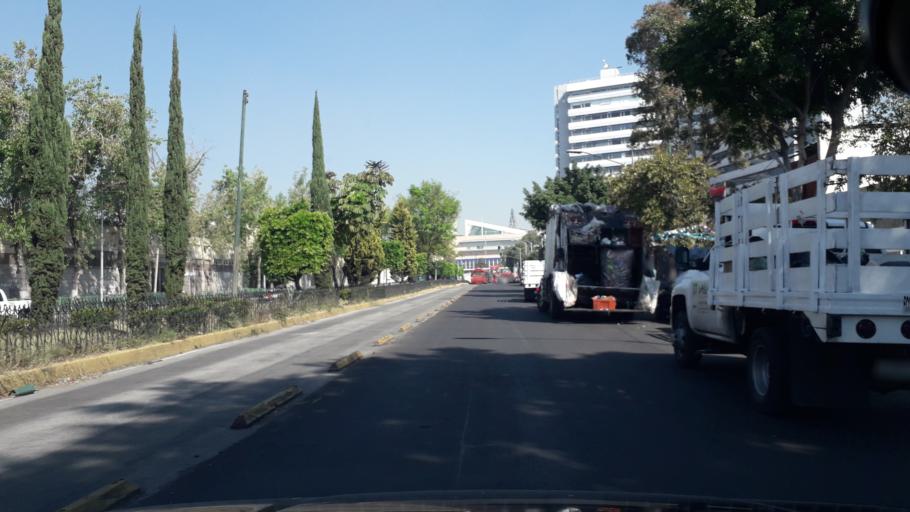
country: MX
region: Mexico City
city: Cuauhtemoc
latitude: 19.4429
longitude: -99.1523
